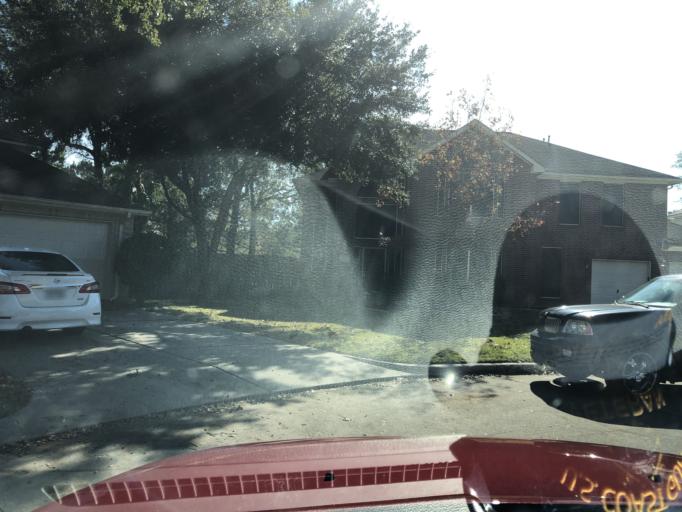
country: US
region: Texas
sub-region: Harris County
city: Tomball
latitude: 30.0245
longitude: -95.5553
